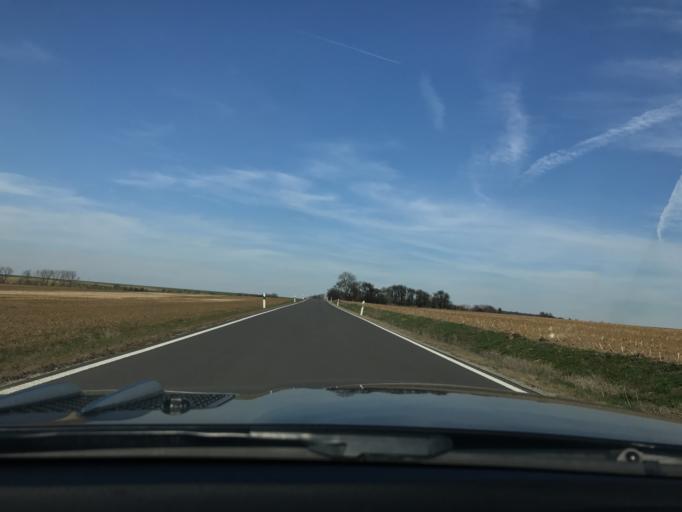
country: DE
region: Thuringia
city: Issersheilingen
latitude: 51.1984
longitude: 10.6388
